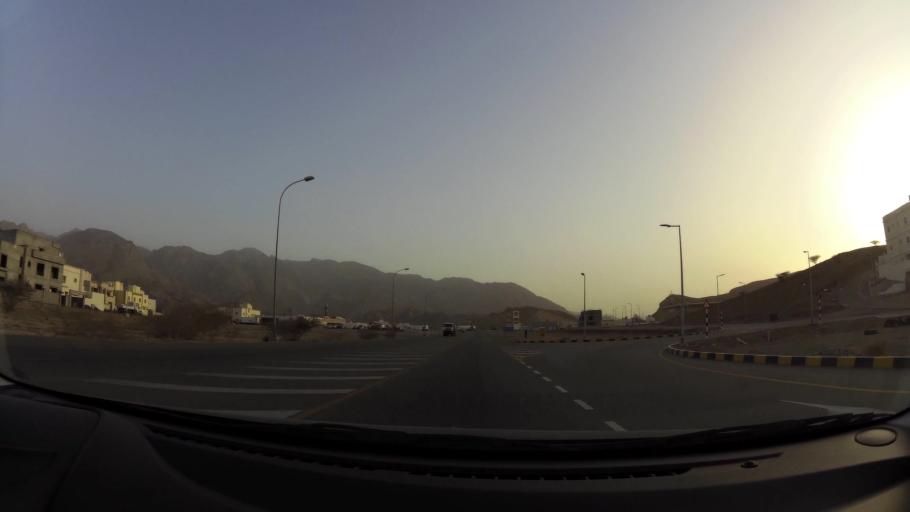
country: OM
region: Muhafazat Masqat
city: Bawshar
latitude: 23.4835
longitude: 58.3110
